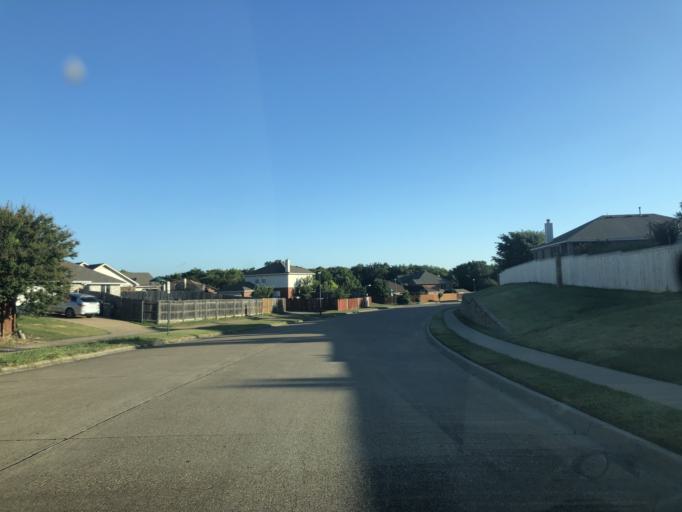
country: US
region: Texas
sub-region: Dallas County
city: Duncanville
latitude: 32.6476
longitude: -96.9519
